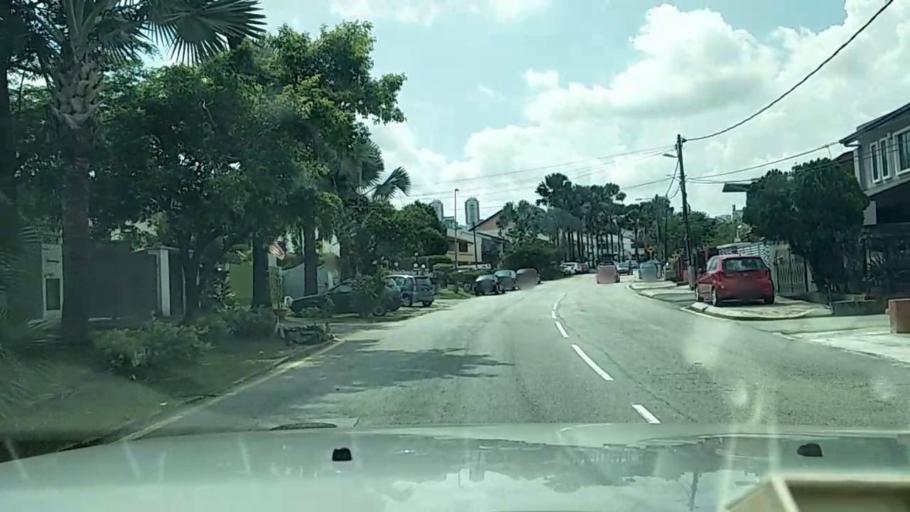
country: MY
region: Kuala Lumpur
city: Kuala Lumpur
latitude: 3.1298
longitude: 101.6740
